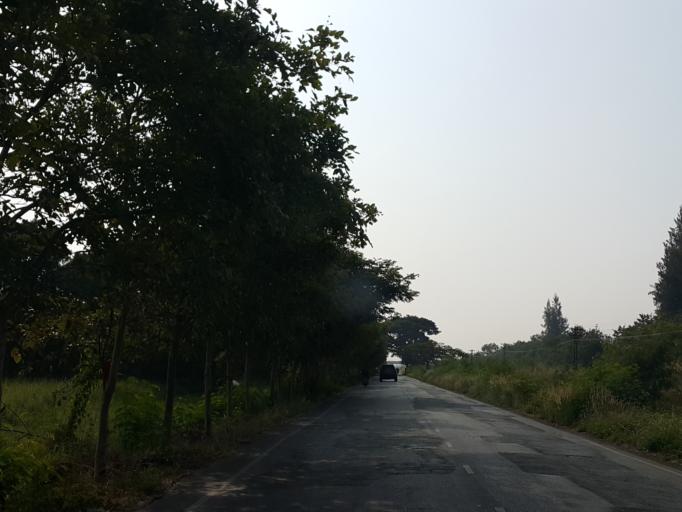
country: TH
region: Chiang Mai
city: Saraphi
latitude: 18.7584
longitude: 99.0213
